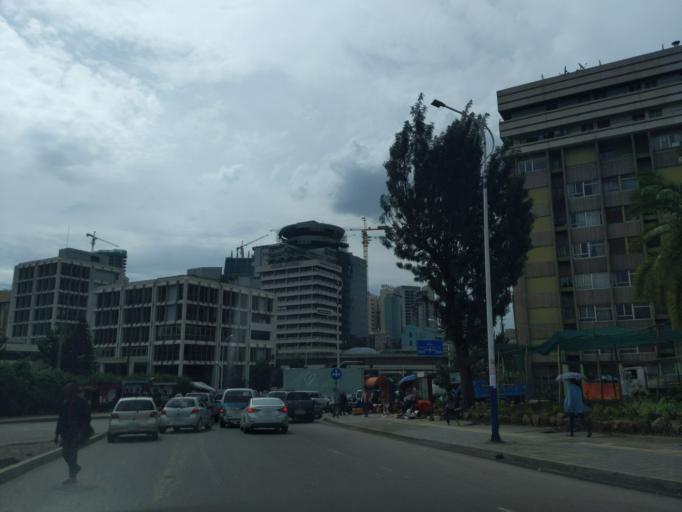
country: ET
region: Adis Abeba
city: Addis Ababa
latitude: 9.0108
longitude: 38.7536
